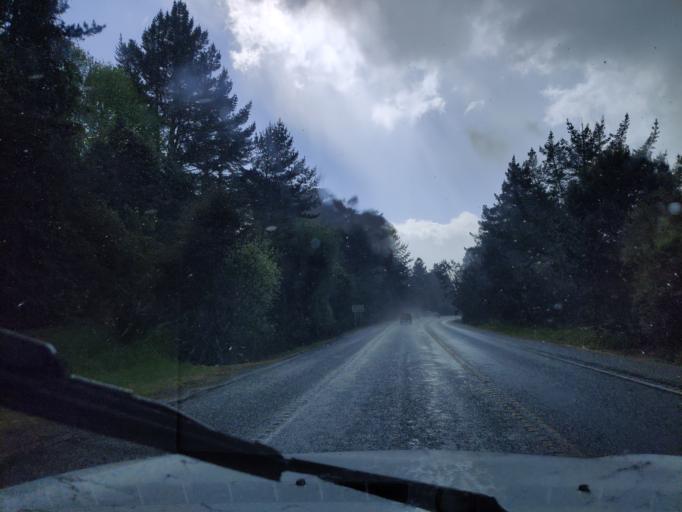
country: NZ
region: Waikato
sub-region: Waipa District
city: Cambridge
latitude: -37.9478
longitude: 175.6094
